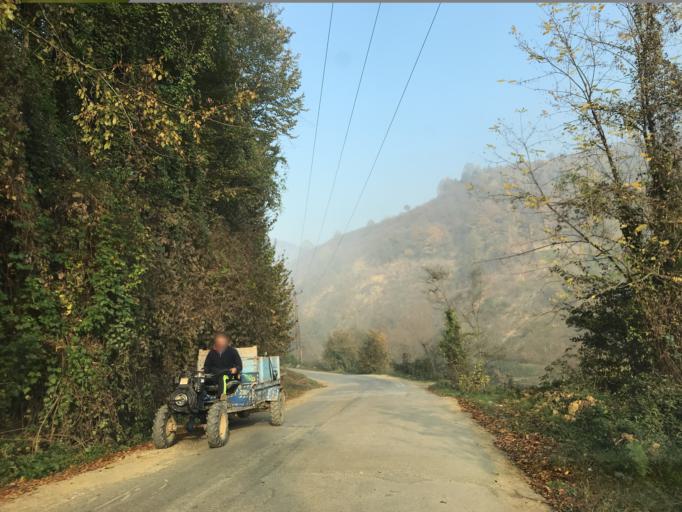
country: TR
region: Duzce
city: Cumayeri
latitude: 40.9157
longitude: 30.9353
